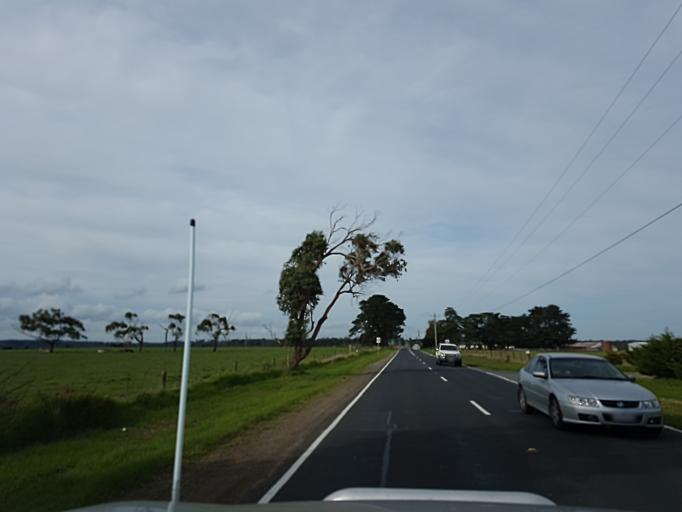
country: AU
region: Victoria
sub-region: Mornington Peninsula
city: Moorooduc
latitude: -38.2493
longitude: 145.1101
